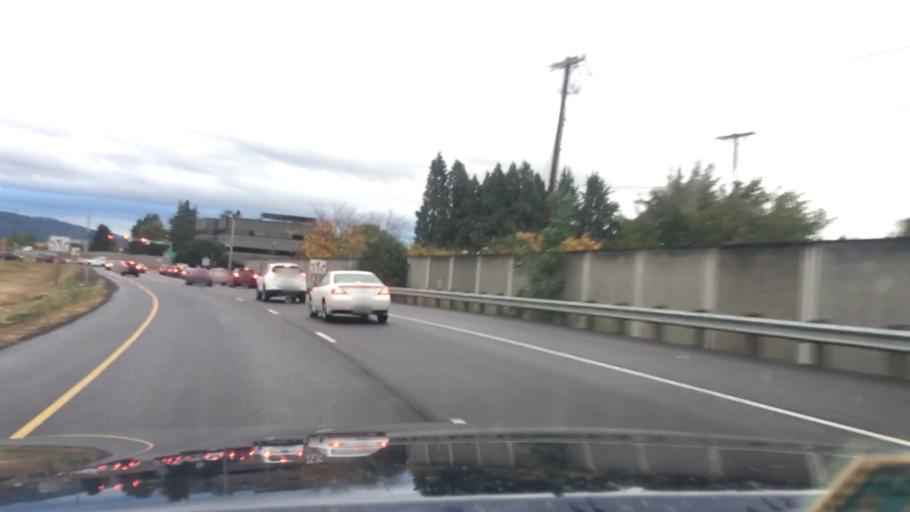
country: US
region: Oregon
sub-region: Lane County
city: Eugene
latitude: 44.0871
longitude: -123.0700
